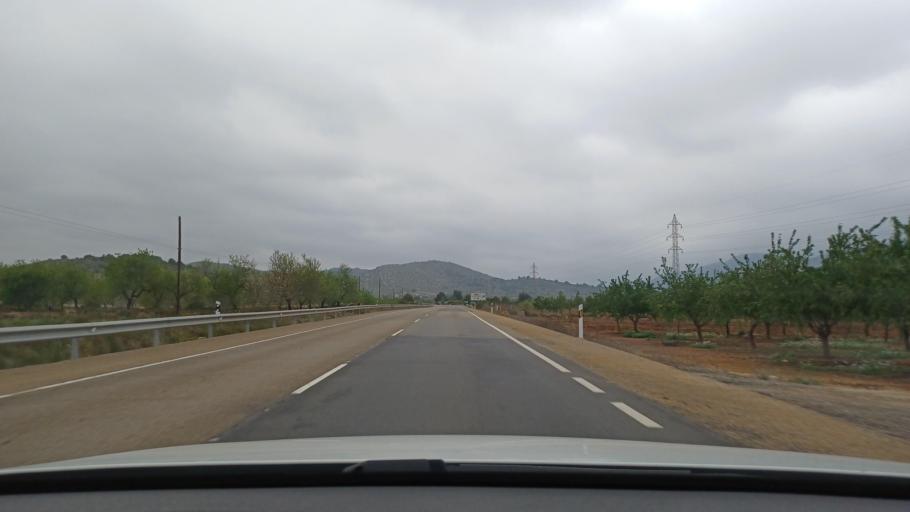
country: ES
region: Valencia
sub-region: Provincia de Castello
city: Alcala de Xivert
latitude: 40.2600
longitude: 0.2384
